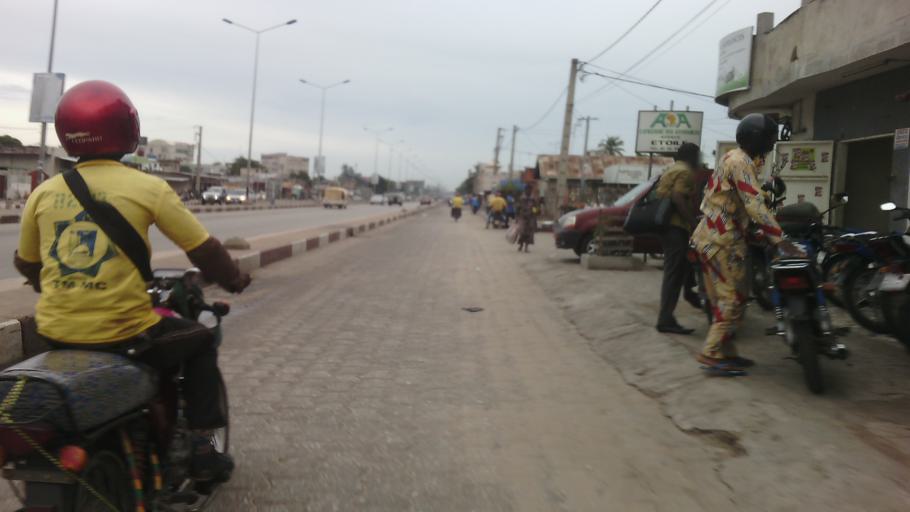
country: BJ
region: Littoral
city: Cotonou
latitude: 6.3696
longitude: 2.4110
